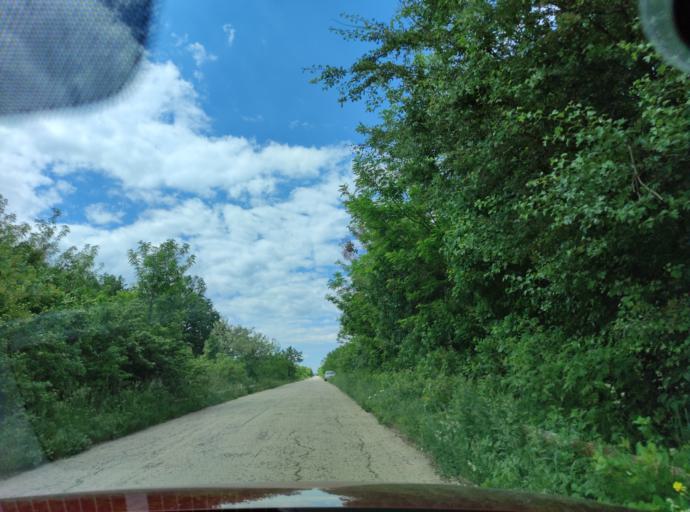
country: BG
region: Montana
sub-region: Obshtina Berkovitsa
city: Berkovitsa
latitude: 43.3611
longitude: 23.0903
